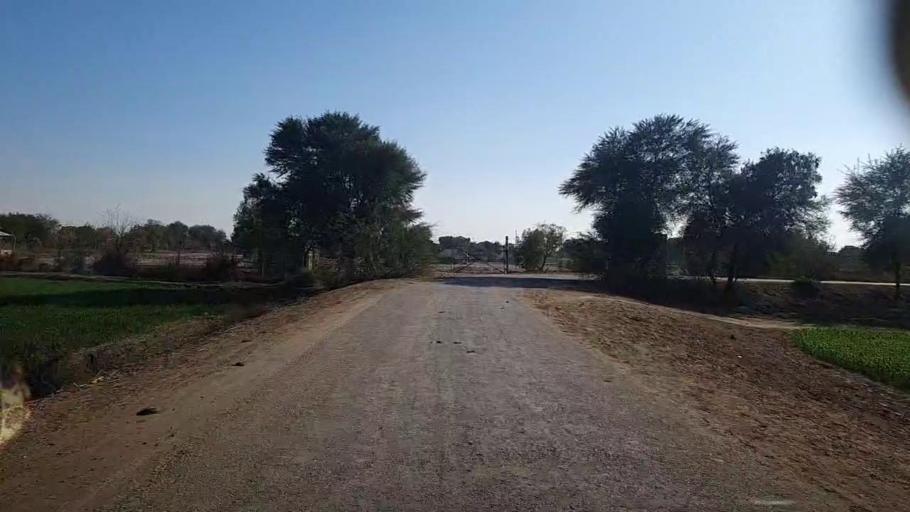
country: PK
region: Sindh
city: Khairpur
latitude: 27.9145
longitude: 69.7519
